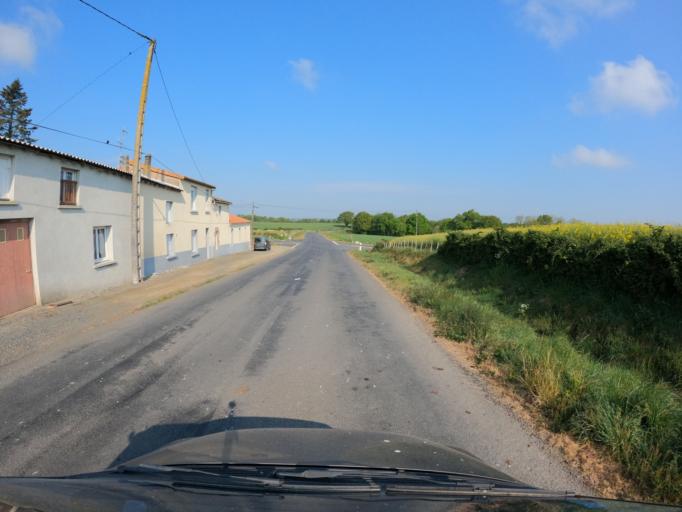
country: FR
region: Pays de la Loire
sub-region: Departement de Maine-et-Loire
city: Roussay
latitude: 47.0781
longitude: -1.0707
